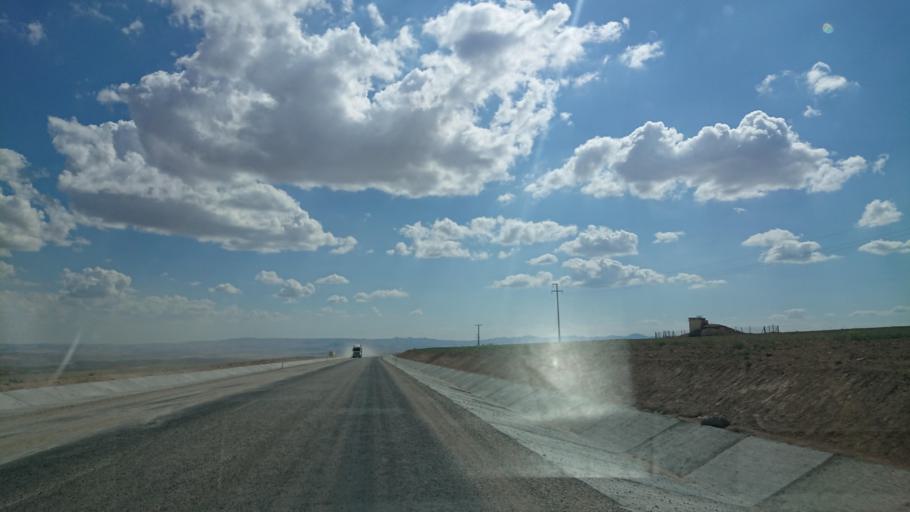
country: TR
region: Kirsehir
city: Kirsehir
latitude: 39.1290
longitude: 34.0371
